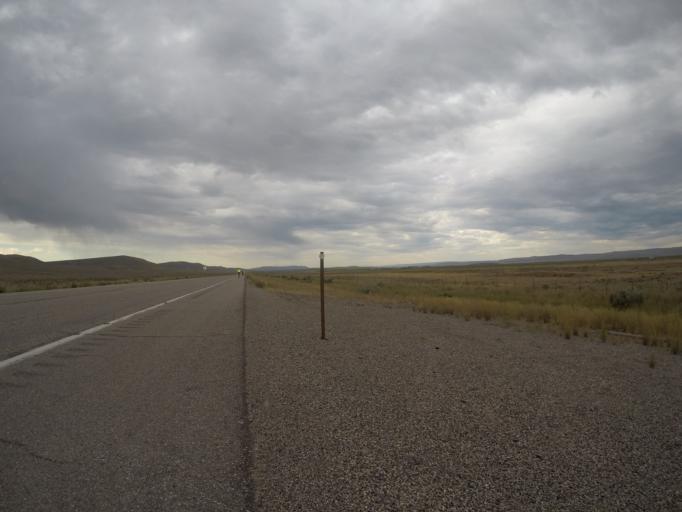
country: US
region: Utah
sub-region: Rich County
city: Randolph
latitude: 41.9088
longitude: -110.9557
